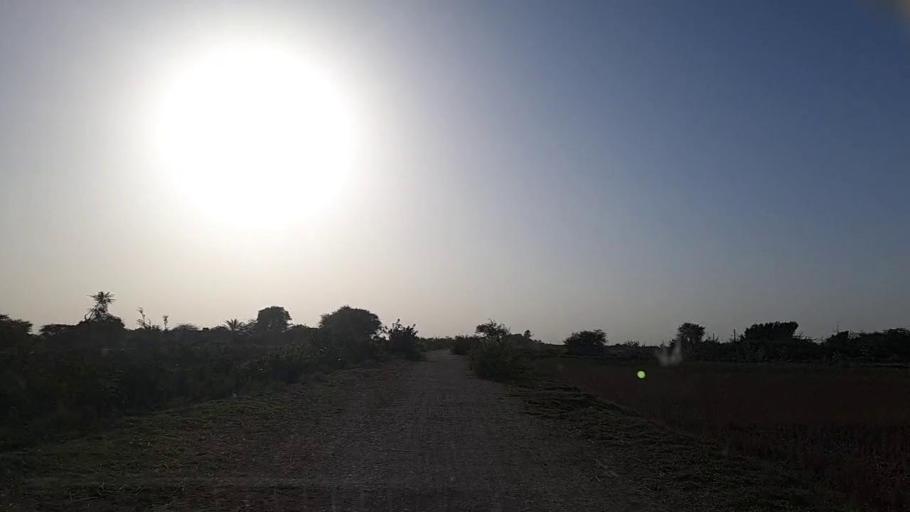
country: PK
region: Sindh
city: Jati
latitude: 24.4167
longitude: 68.2997
